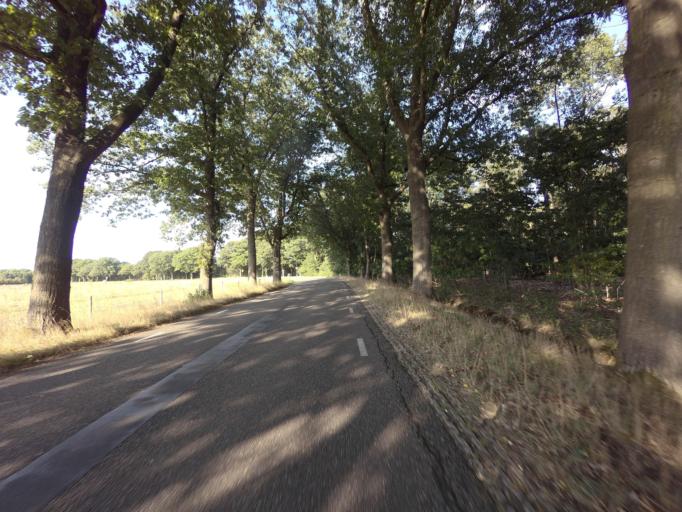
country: NL
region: North Brabant
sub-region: Gemeente Heeze-Leende
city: Heeze
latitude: 51.3726
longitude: 5.6249
